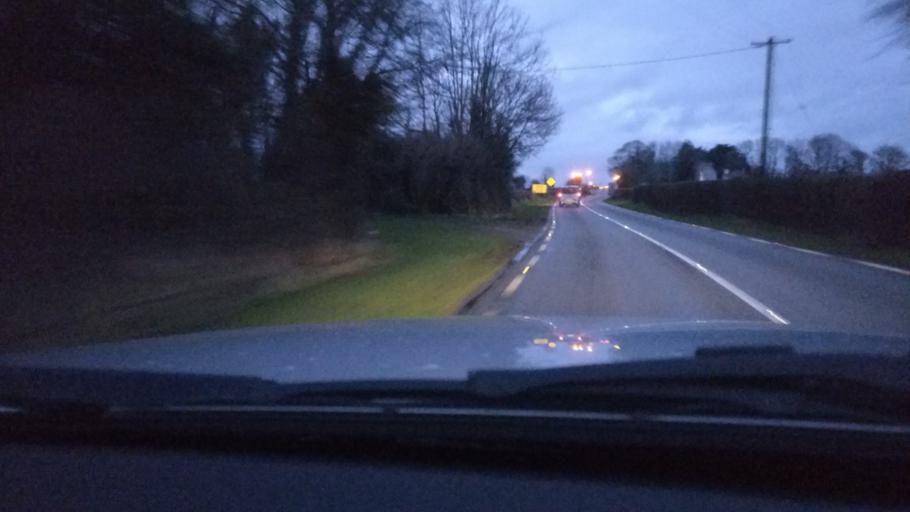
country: IE
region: Leinster
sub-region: An Longfort
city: Ballymahon
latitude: 53.5267
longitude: -7.7947
